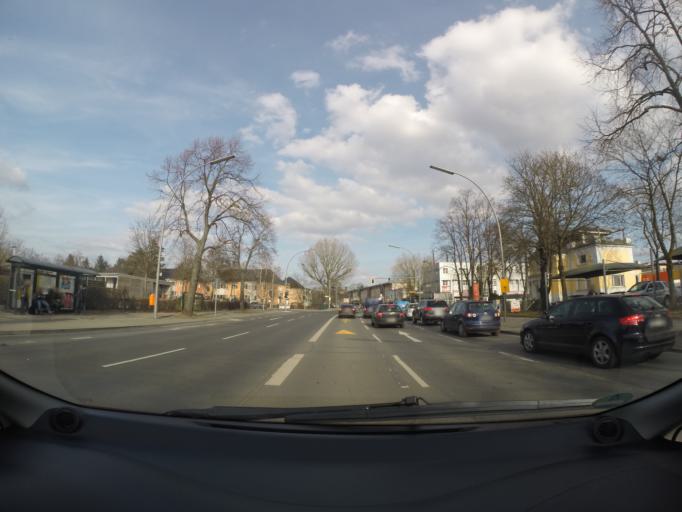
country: DE
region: Berlin
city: Lichterfelde
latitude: 52.4191
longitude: 13.2922
